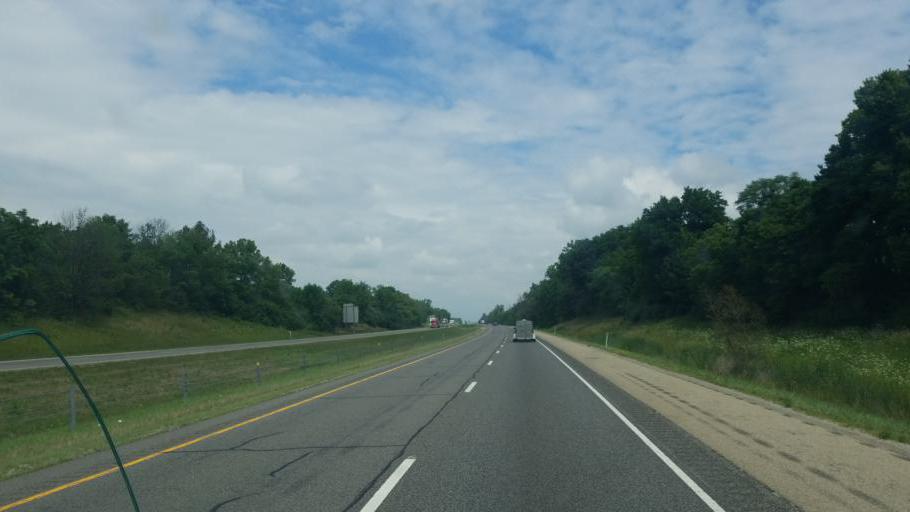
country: US
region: Indiana
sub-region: Delaware County
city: Yorktown
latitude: 40.2367
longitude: -85.5571
